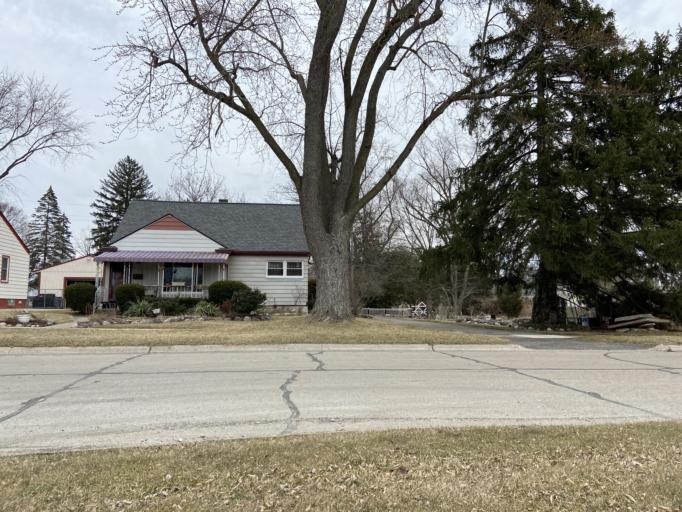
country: US
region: Michigan
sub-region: Oakland County
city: Farmington
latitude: 42.4566
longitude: -83.3552
